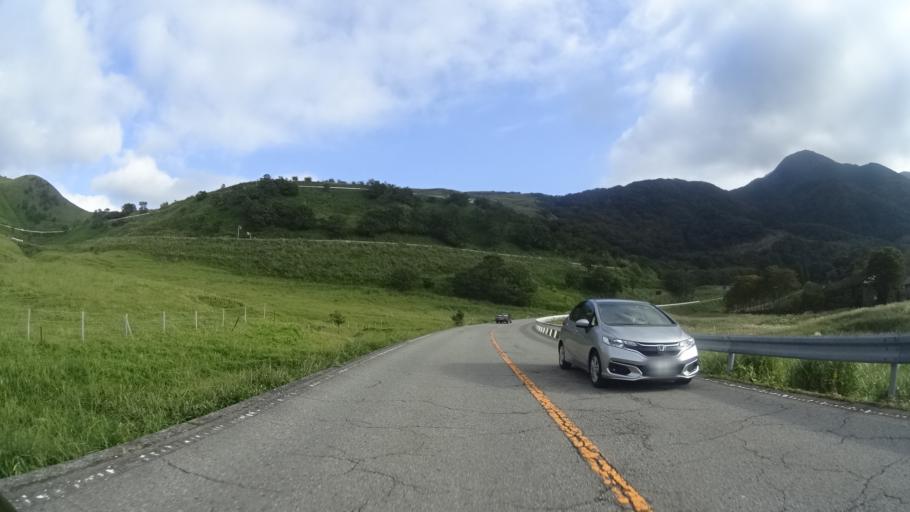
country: JP
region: Oita
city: Beppu
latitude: 33.2623
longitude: 131.3800
